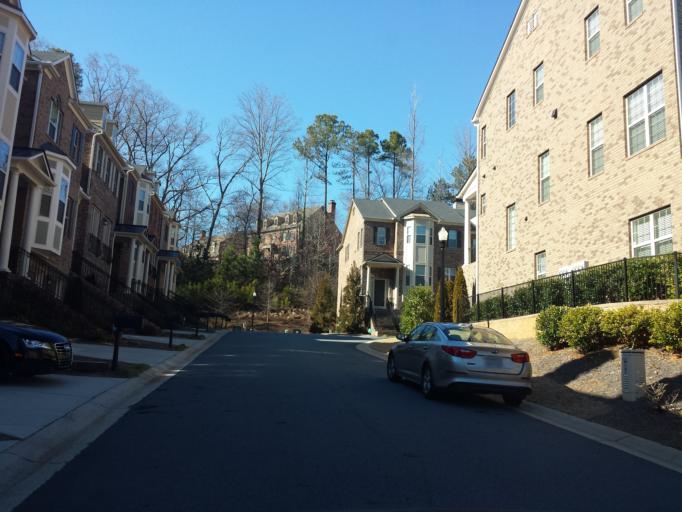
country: US
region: Georgia
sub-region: Cobb County
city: Vinings
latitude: 33.9078
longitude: -84.4616
